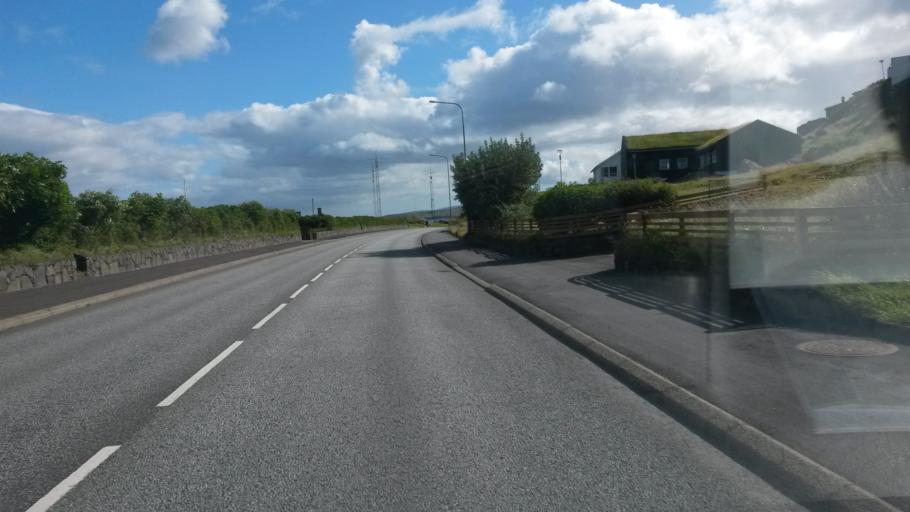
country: FO
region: Streymoy
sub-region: Torshavn
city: Torshavn
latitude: 62.0176
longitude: -6.7559
